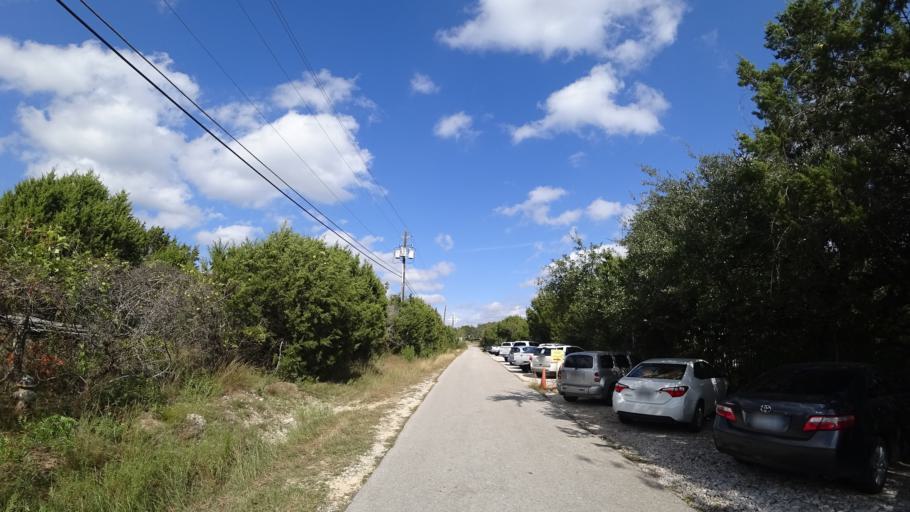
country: US
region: Texas
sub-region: Travis County
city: Barton Creek
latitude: 30.2572
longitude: -97.8914
